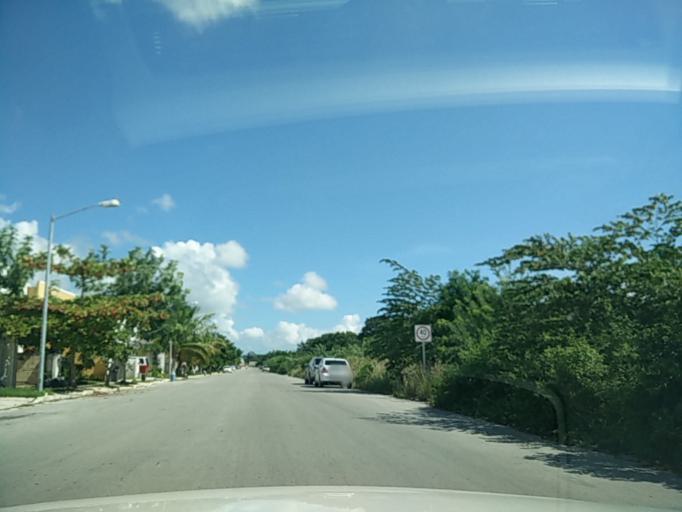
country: MX
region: Quintana Roo
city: Playa del Carmen
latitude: 20.6577
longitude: -87.0650
